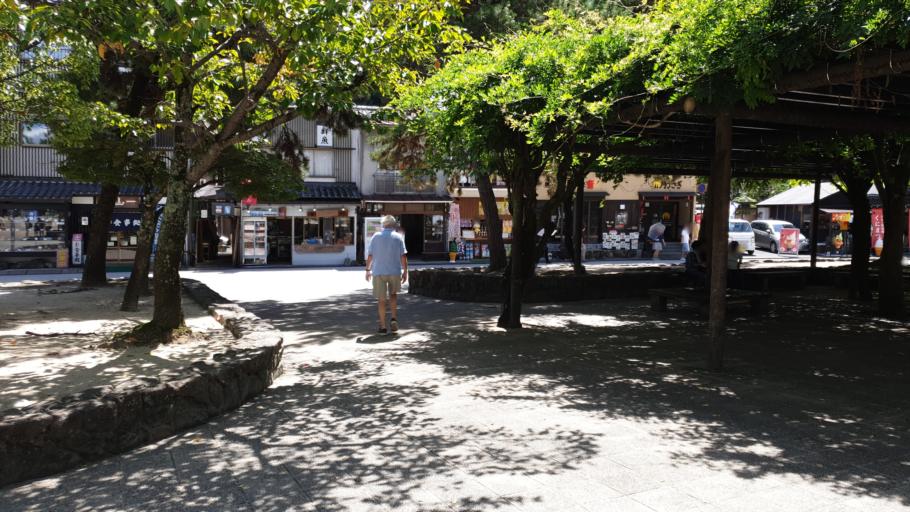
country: JP
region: Hiroshima
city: Miyajima
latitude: 34.3015
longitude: 132.3222
